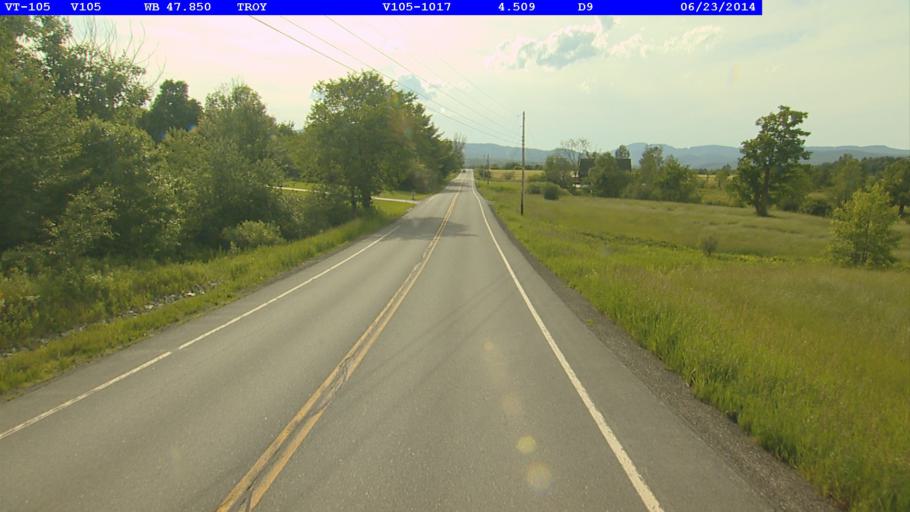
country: US
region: Vermont
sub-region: Orleans County
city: Newport
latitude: 44.9893
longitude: -72.3681
